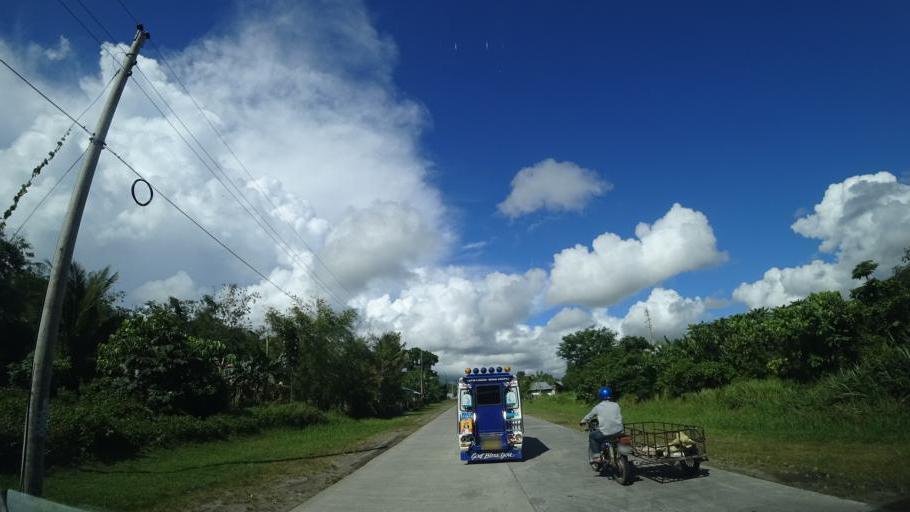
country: PH
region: Eastern Visayas
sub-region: Province of Leyte
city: Palo
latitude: 11.1536
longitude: 125.0011
